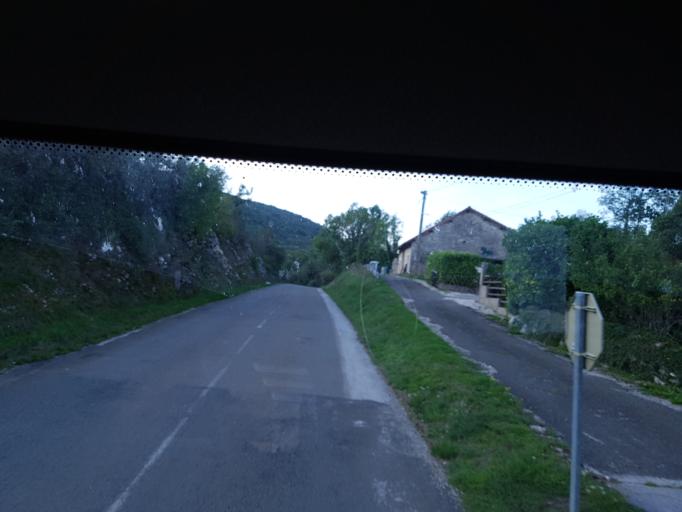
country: FR
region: Franche-Comte
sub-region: Departement du Jura
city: Moirans-en-Montagne
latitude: 46.4057
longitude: 5.6487
